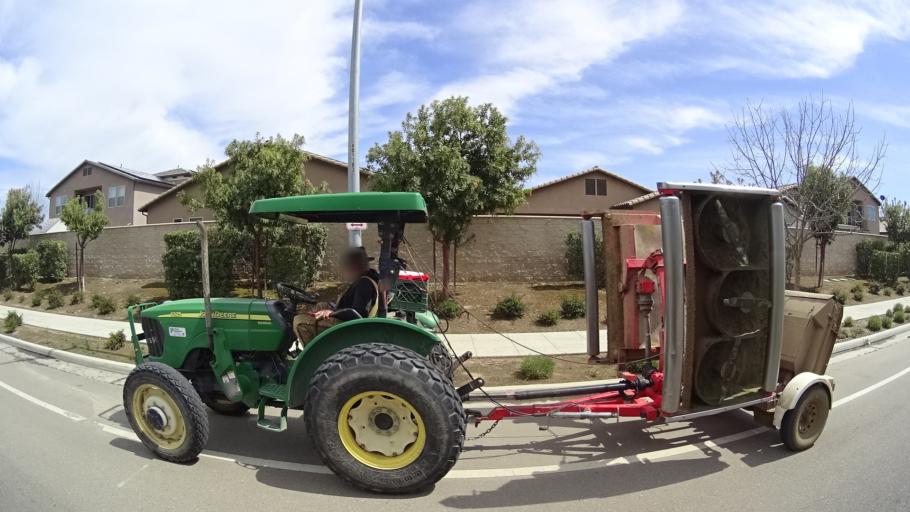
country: US
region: California
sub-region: Fresno County
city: Biola
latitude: 36.8173
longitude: -119.9256
